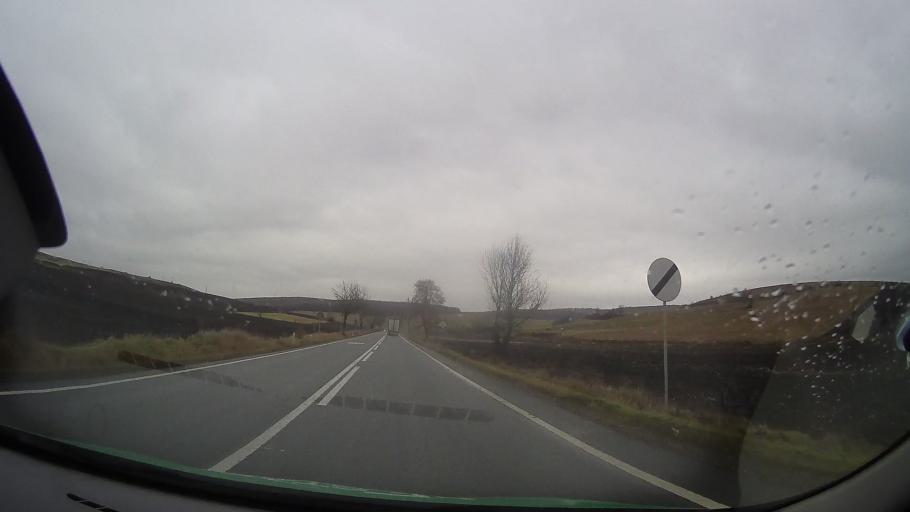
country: RO
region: Mures
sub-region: Comuna Lunca
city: Lunca
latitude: 46.8683
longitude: 24.5536
